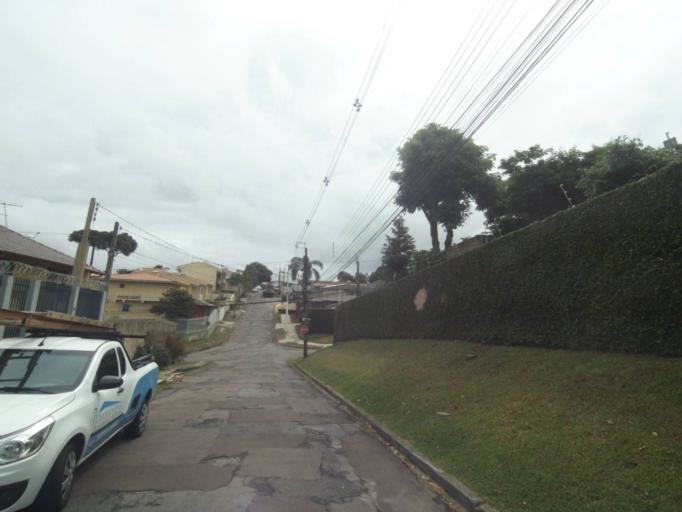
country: BR
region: Parana
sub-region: Curitiba
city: Curitiba
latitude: -25.4464
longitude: -49.3436
